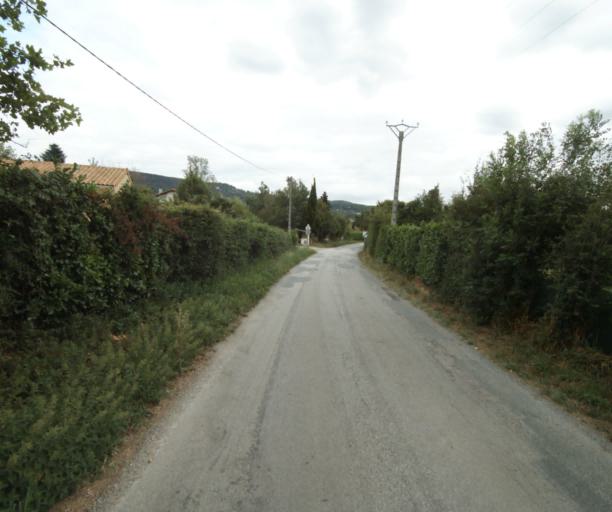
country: FR
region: Midi-Pyrenees
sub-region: Departement du Tarn
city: Soreze
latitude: 43.4558
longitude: 2.0548
